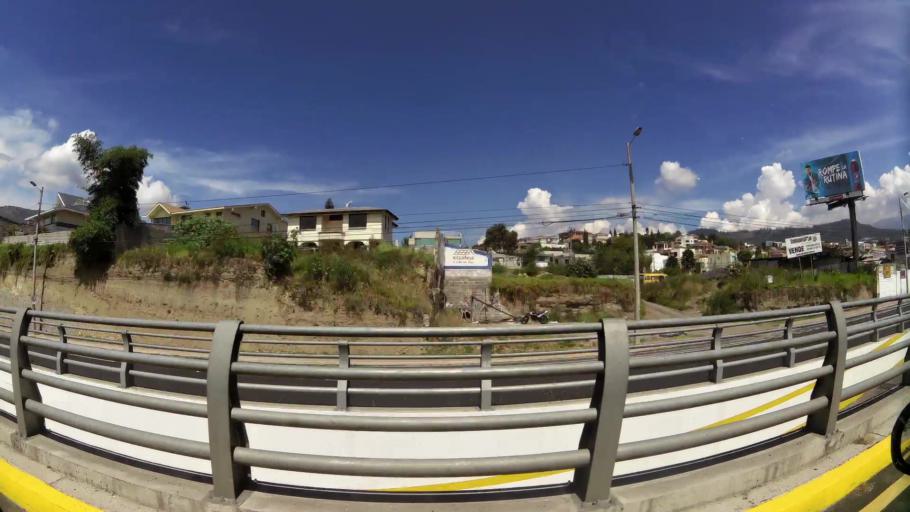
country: EC
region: Pichincha
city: Quito
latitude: -0.2076
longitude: -78.4263
